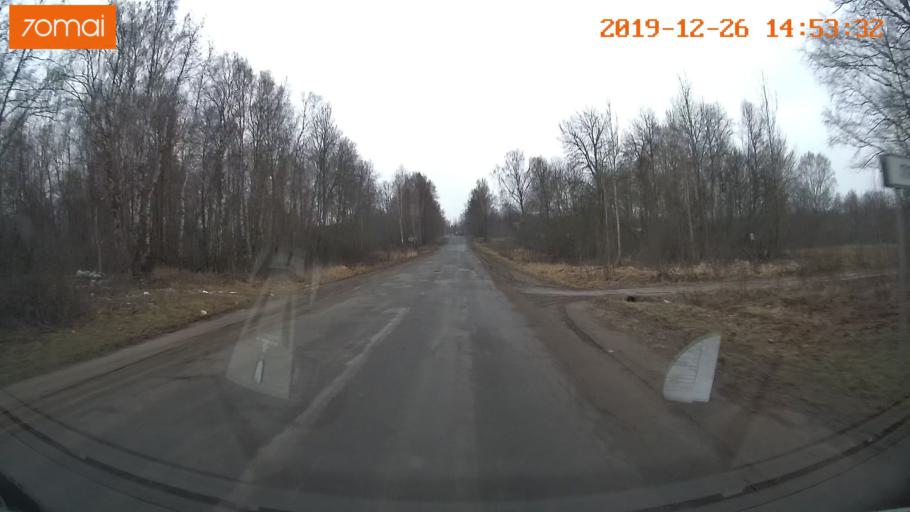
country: RU
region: Jaroslavl
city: Rybinsk
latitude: 58.3143
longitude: 38.8886
